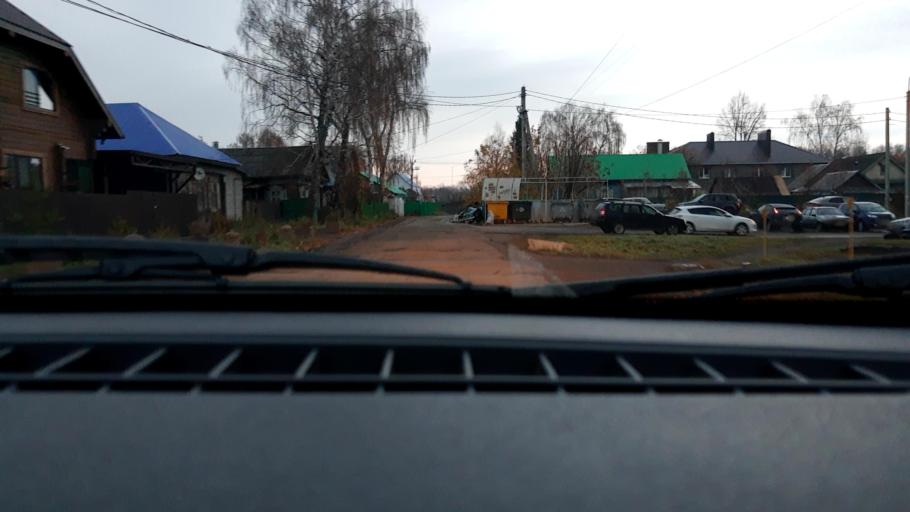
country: RU
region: Bashkortostan
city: Mikhaylovka
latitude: 54.7857
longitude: 55.8883
